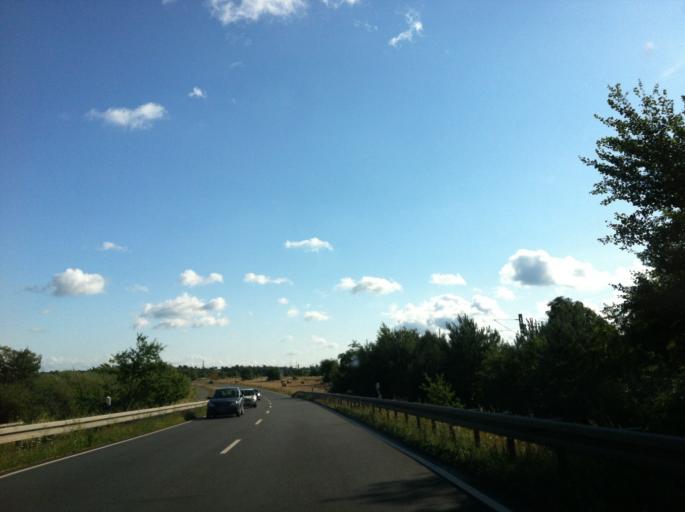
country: DE
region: Hesse
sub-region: Regierungsbezirk Darmstadt
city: Darmstadt
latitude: 49.9009
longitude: 8.6400
